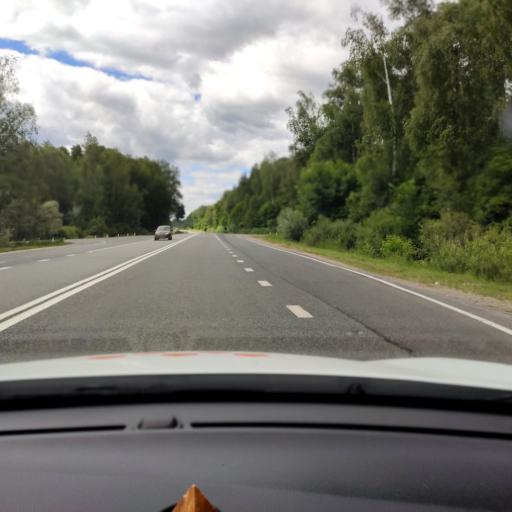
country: RU
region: Tatarstan
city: Aysha
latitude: 55.8887
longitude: 48.5970
